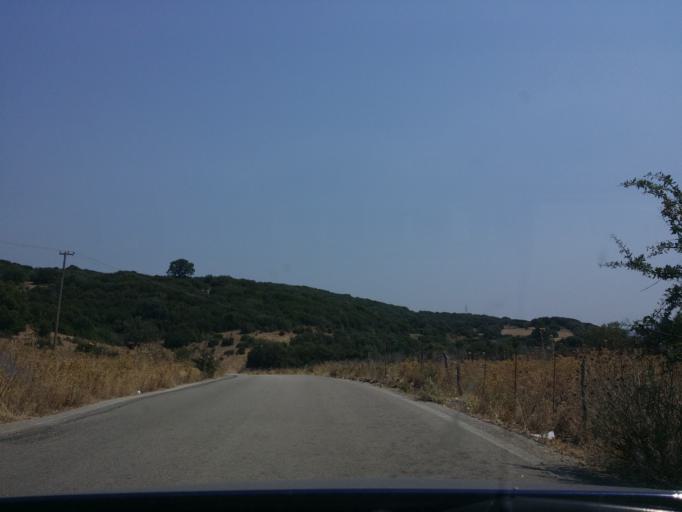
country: GR
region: West Greece
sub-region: Nomos Aitolias kai Akarnanias
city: Katouna
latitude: 38.7771
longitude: 21.0989
